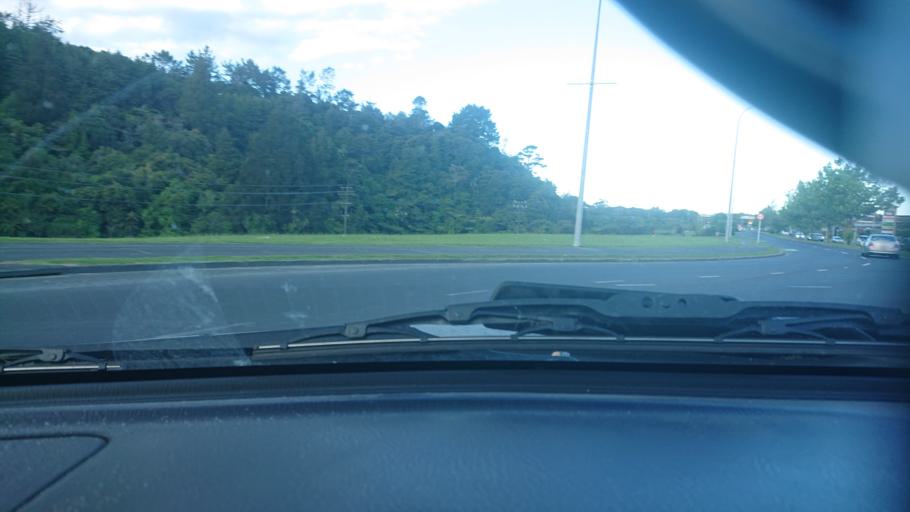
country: NZ
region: Auckland
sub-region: Auckland
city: Rothesay Bay
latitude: -36.7205
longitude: 174.7084
